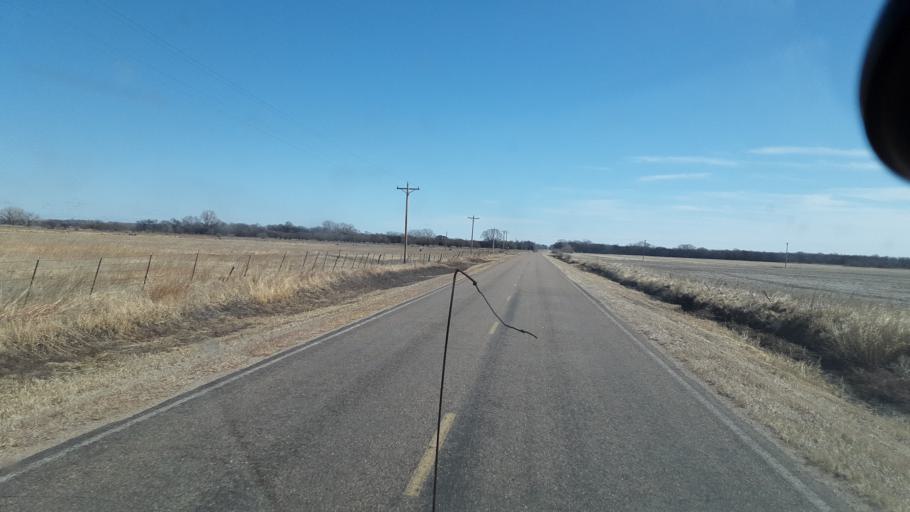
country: US
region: Kansas
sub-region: Reno County
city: Nickerson
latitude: 38.2175
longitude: -98.0728
